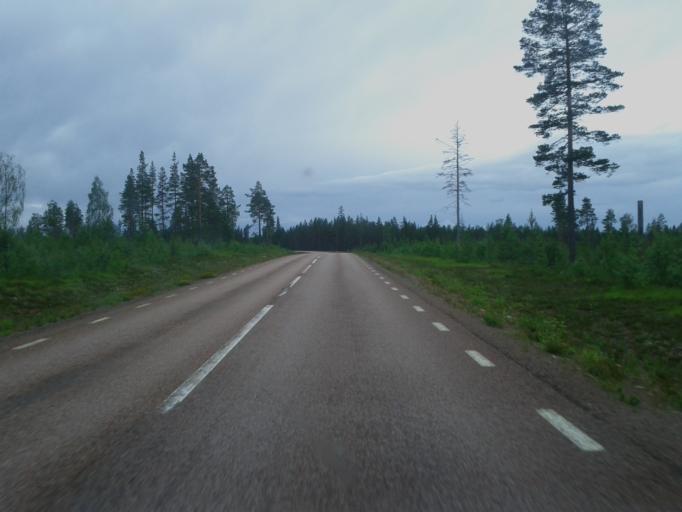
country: SE
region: Dalarna
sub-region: Alvdalens Kommun
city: AElvdalen
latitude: 61.4685
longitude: 13.4231
